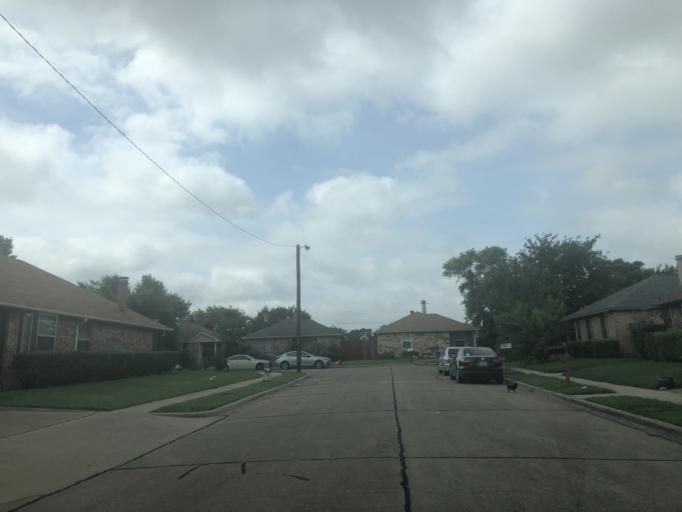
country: US
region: Texas
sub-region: Dallas County
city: Irving
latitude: 32.8031
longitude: -96.9641
